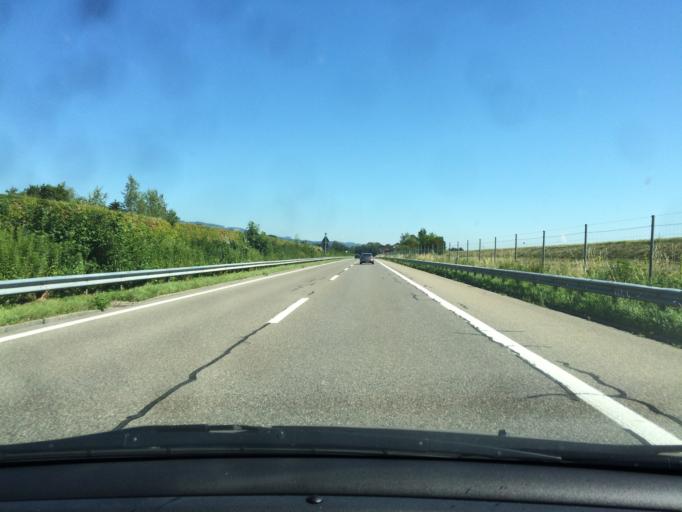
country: AT
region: Vorarlberg
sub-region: Politischer Bezirk Feldkirch
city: Koblach
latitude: 47.3396
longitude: 9.5943
